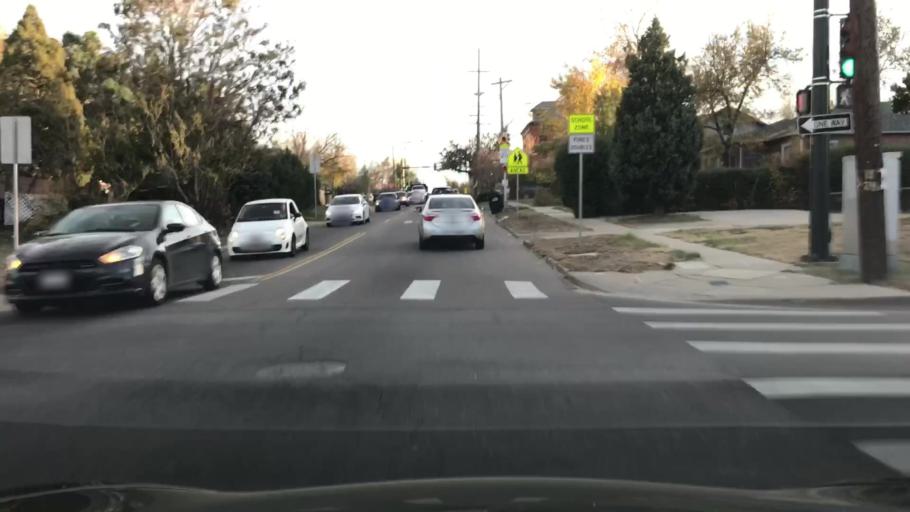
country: US
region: Colorado
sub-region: Arapahoe County
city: Glendale
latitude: 39.7388
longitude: -104.9035
